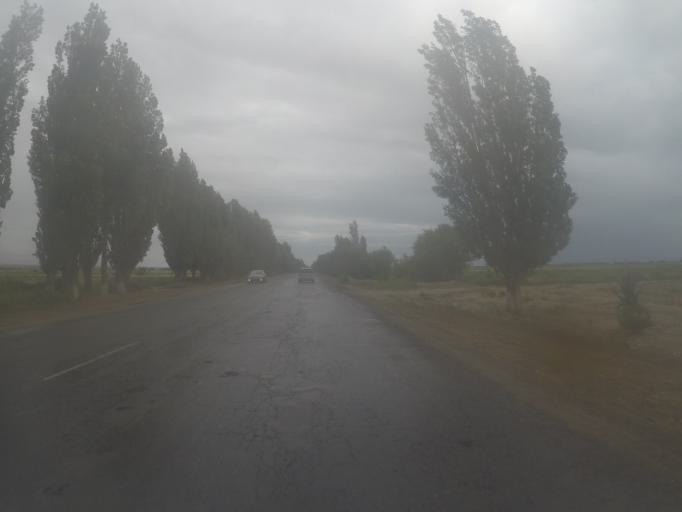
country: KG
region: Ysyk-Koel
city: Balykchy
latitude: 42.4929
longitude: 76.3340
